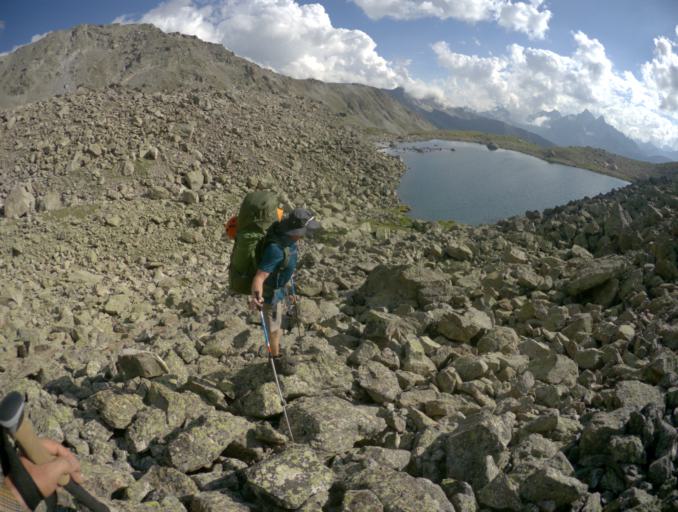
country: RU
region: Karachayevo-Cherkesiya
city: Uchkulan
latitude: 43.3146
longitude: 42.0691
